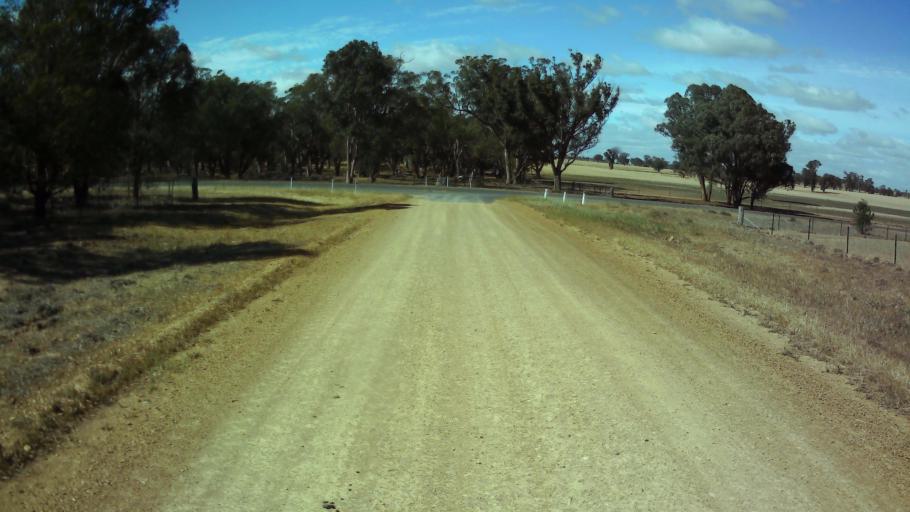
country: AU
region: New South Wales
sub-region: Weddin
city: Grenfell
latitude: -34.0648
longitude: 148.3113
